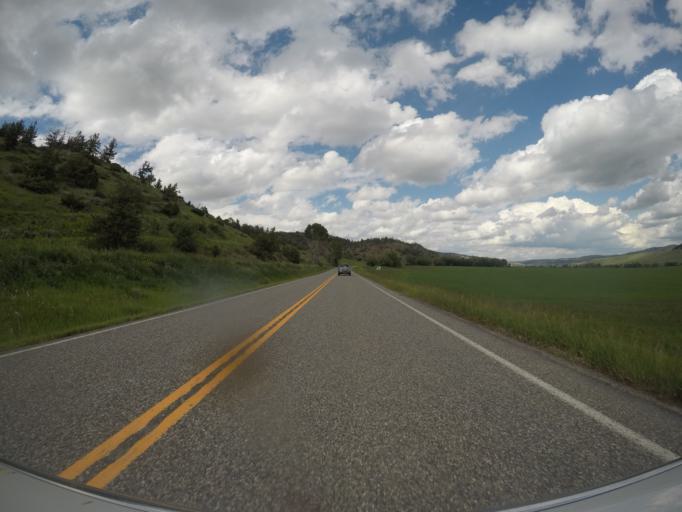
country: US
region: Montana
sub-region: Sweet Grass County
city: Big Timber
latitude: 45.6818
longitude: -110.0854
